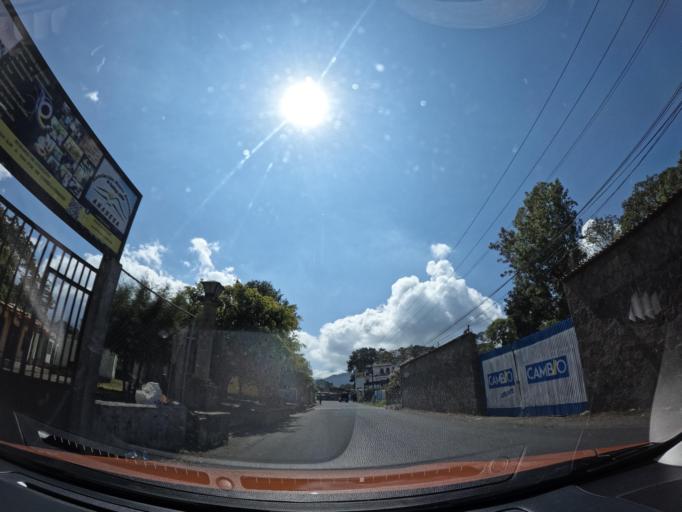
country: GT
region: Solola
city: Santiago Atitlan
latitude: 14.6280
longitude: -91.2318
